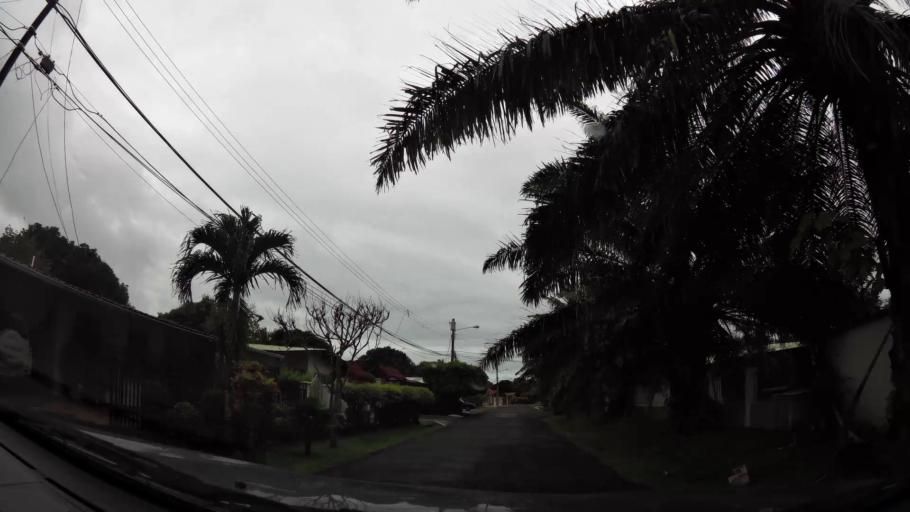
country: PA
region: Chiriqui
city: David
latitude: 8.4361
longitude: -82.4451
